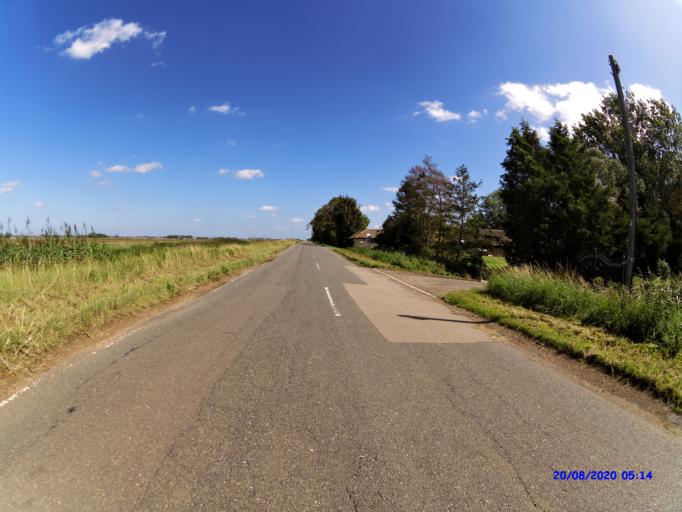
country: GB
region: England
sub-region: Cambridgeshire
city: Whittlesey
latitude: 52.5215
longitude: -0.1187
